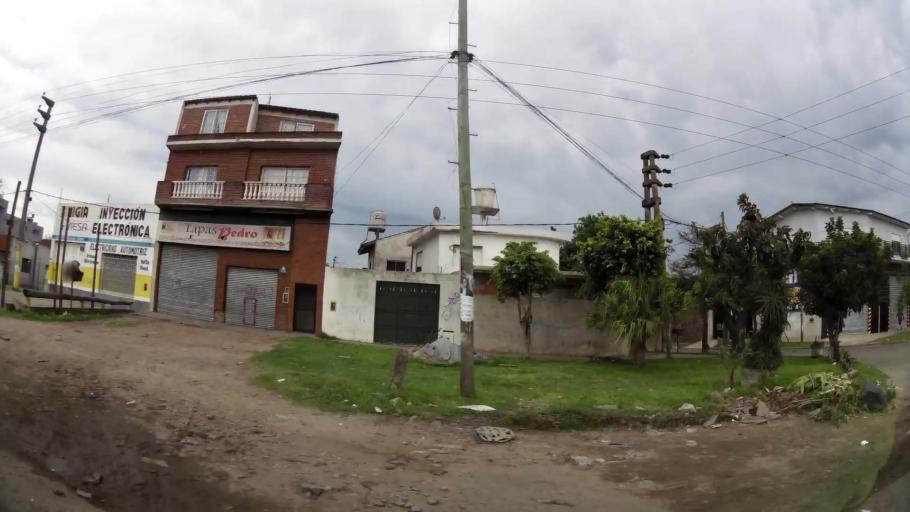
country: AR
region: Buenos Aires
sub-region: Partido de Quilmes
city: Quilmes
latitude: -34.7766
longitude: -58.2807
